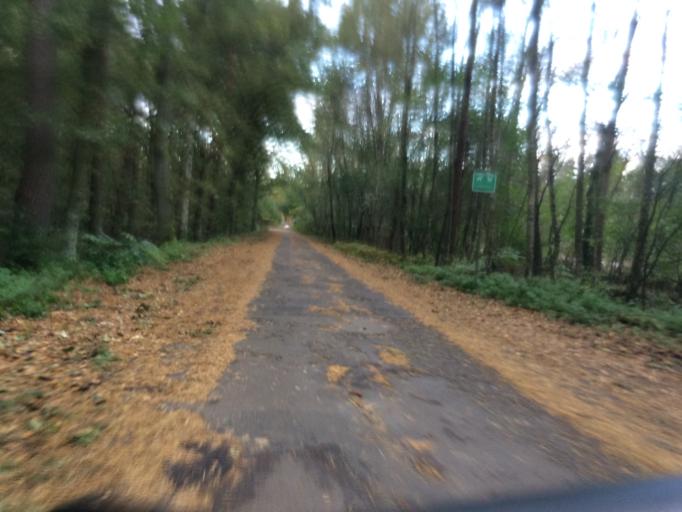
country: DE
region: Brandenburg
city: Birkenwerder
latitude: 52.7029
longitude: 13.3009
